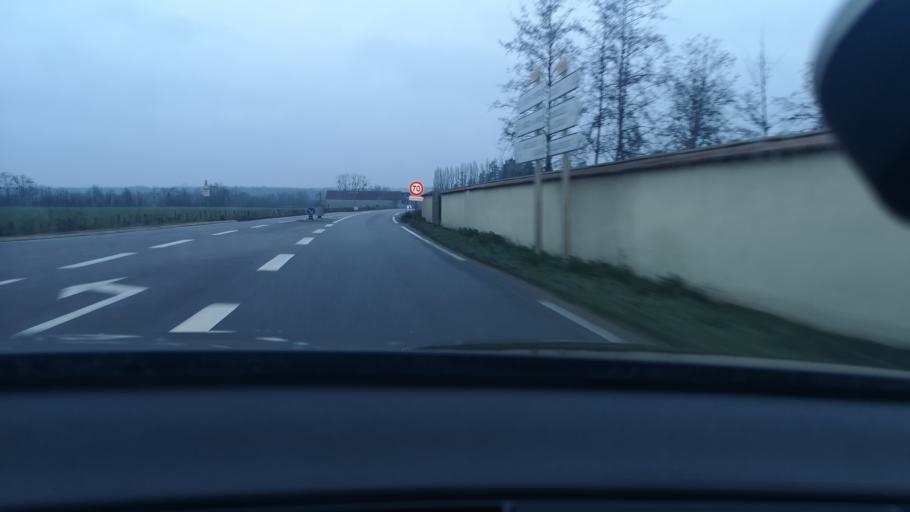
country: FR
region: Bourgogne
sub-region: Departement de la Cote-d'Or
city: Aiserey
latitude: 47.1307
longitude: 5.0938
